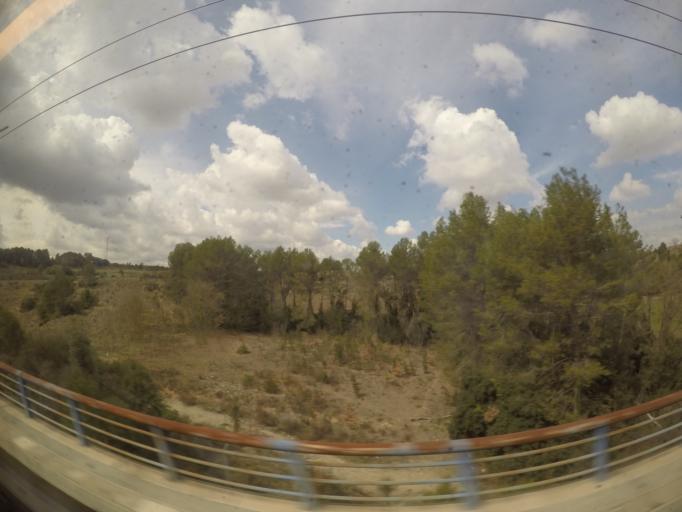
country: ES
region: Catalonia
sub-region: Provincia de Barcelona
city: Sant Llorenc d'Hortons
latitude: 41.4498
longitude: 1.8413
